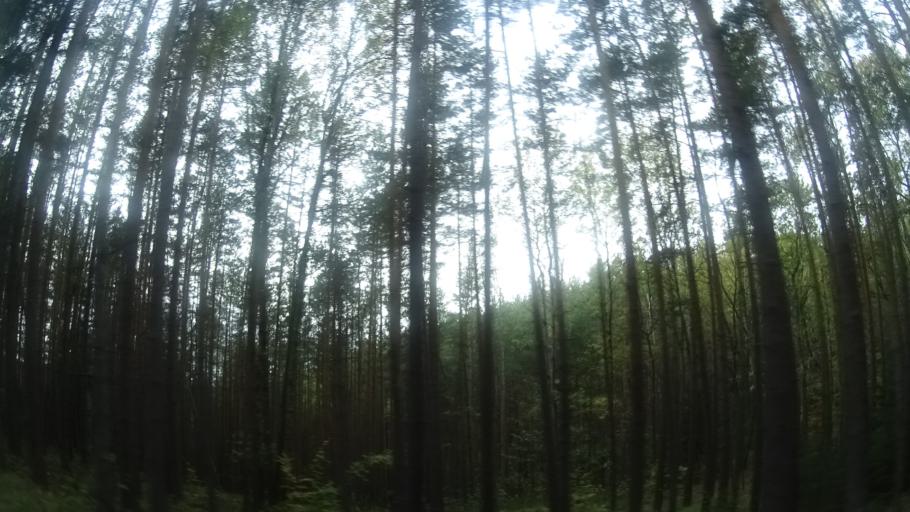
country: DE
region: Thuringia
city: Saalfeld
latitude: 50.6778
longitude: 11.3881
